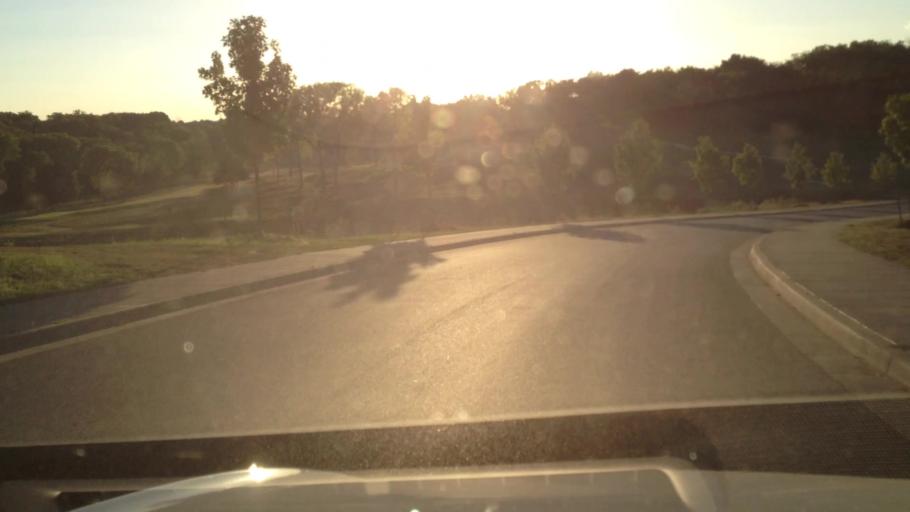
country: US
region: Kansas
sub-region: Douglas County
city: Lawrence
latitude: 38.9547
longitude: -95.2928
